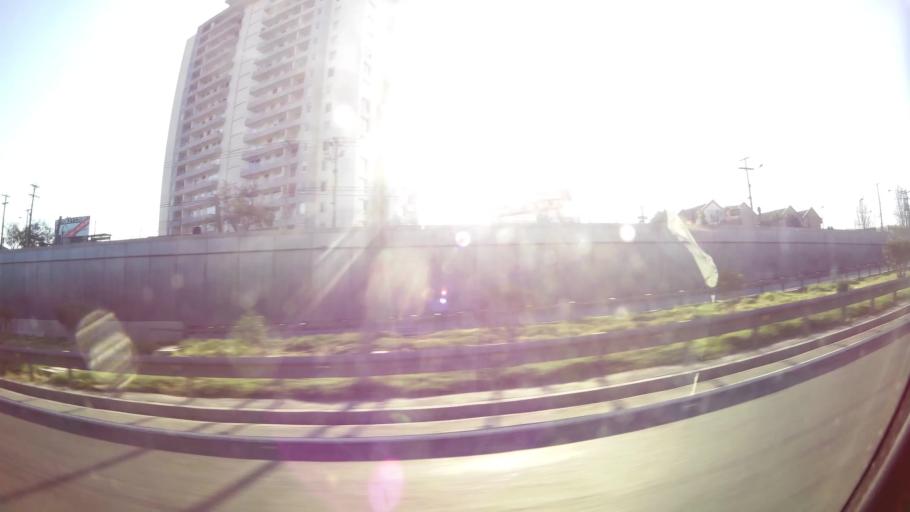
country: CL
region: Santiago Metropolitan
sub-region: Provincia de Santiago
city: Lo Prado
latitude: -33.4706
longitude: -70.7608
